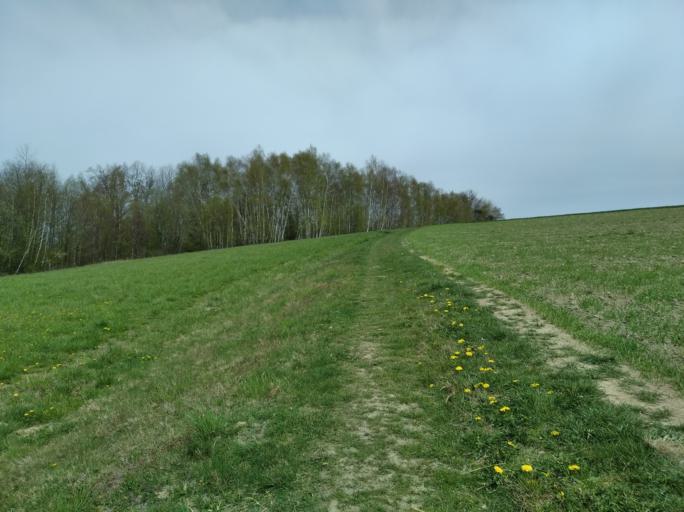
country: PL
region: Subcarpathian Voivodeship
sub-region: Powiat ropczycko-sedziszowski
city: Wielopole Skrzynskie
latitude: 49.9118
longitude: 21.6117
